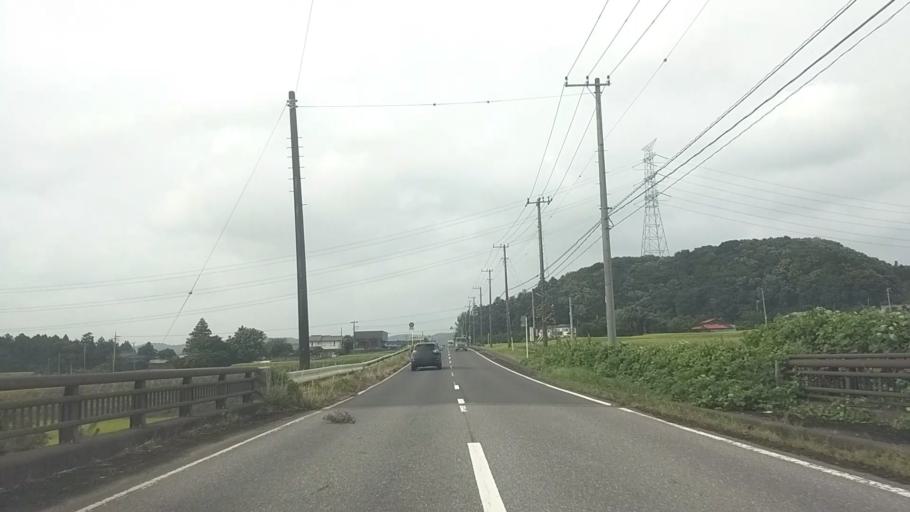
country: JP
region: Chiba
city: Kimitsu
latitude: 35.2808
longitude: 139.9901
